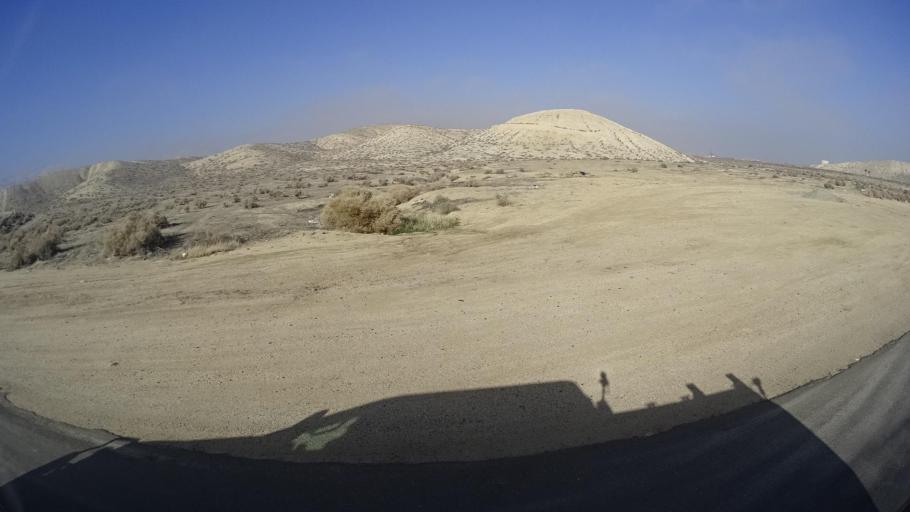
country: US
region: California
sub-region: Kern County
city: Maricopa
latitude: 35.0395
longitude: -119.4239
